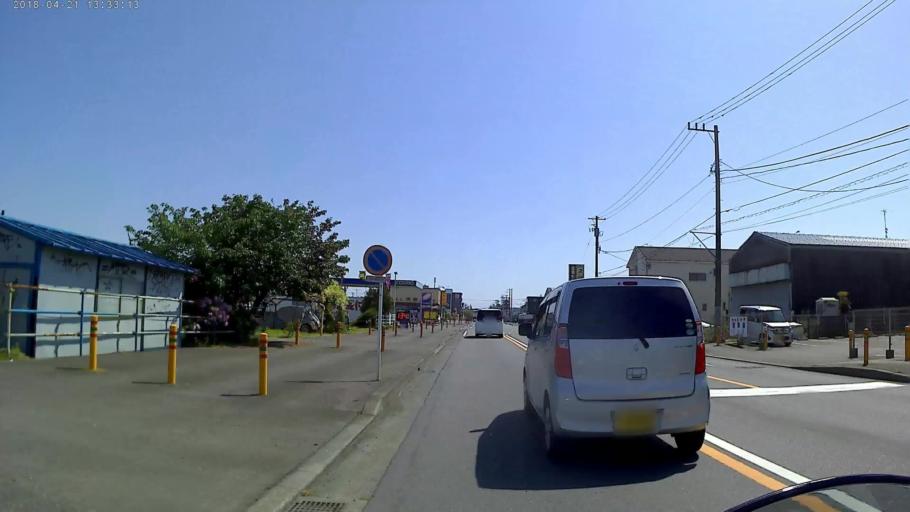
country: JP
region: Kanagawa
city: Atsugi
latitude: 35.3991
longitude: 139.3813
